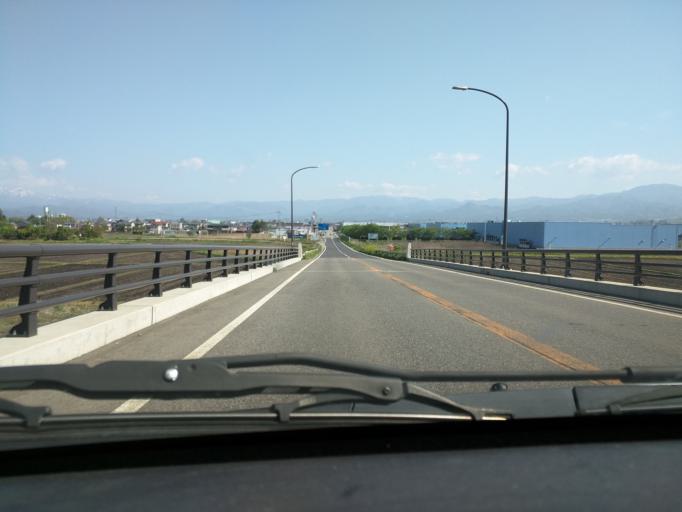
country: JP
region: Fukushima
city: Kitakata
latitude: 37.5833
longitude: 139.8931
